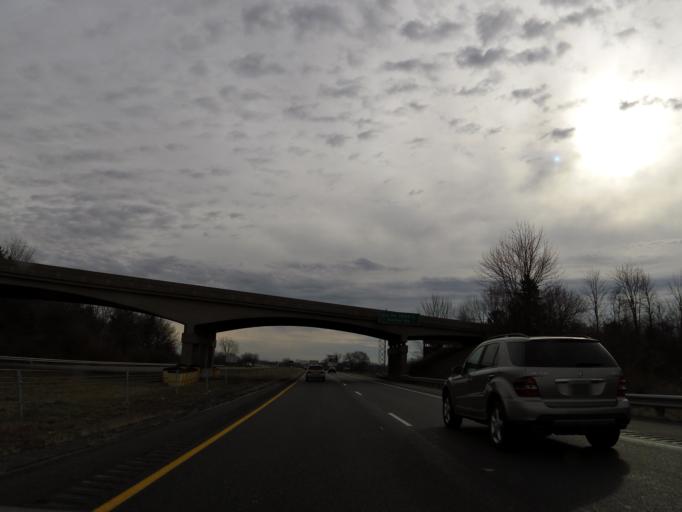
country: US
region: Indiana
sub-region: Hendricks County
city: Fairfield Heights
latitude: 39.8366
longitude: -86.3472
